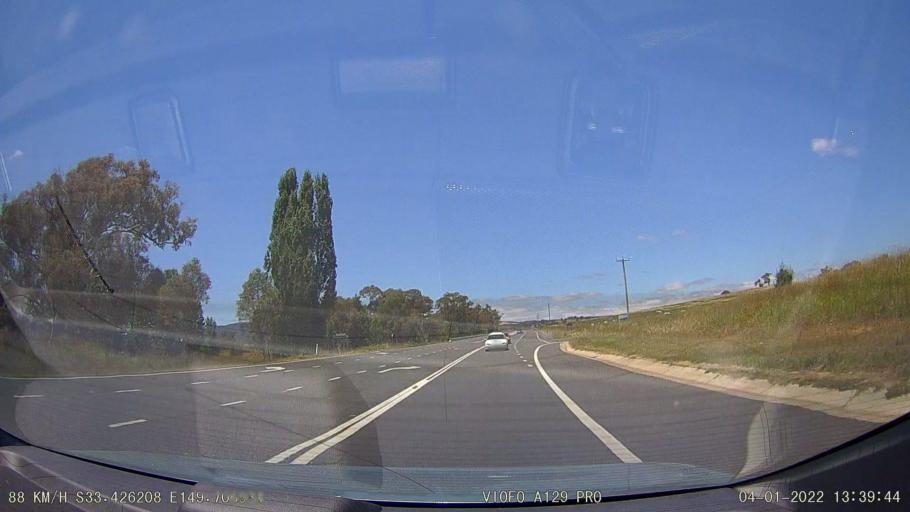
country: AU
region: New South Wales
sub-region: Bathurst Regional
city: Kelso
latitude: -33.4258
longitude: 149.7072
